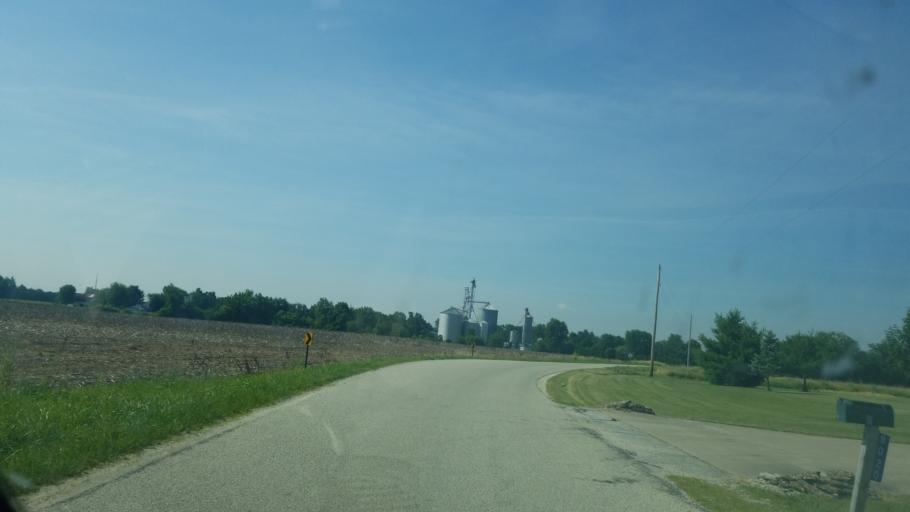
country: US
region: Ohio
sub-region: Wyandot County
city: Carey
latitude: 41.0069
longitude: -83.3244
